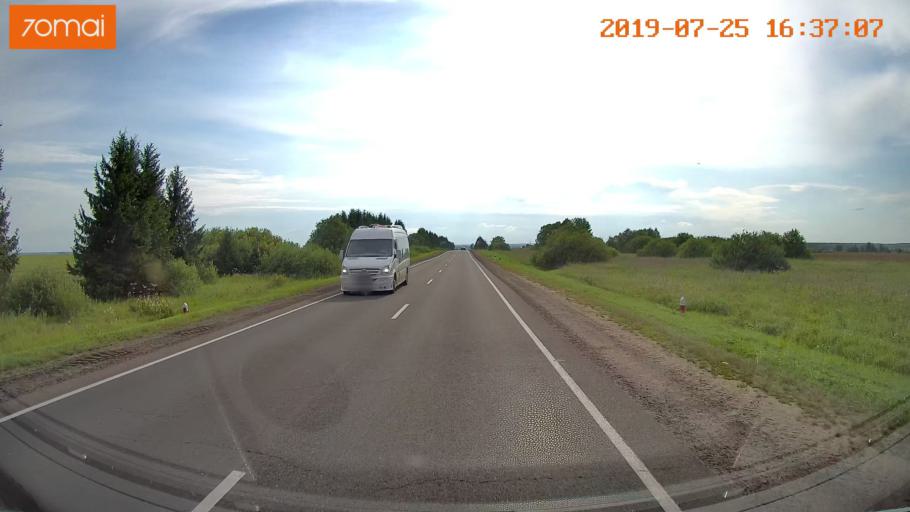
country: RU
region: Ivanovo
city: Privolzhsk
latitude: 57.3922
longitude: 41.3838
